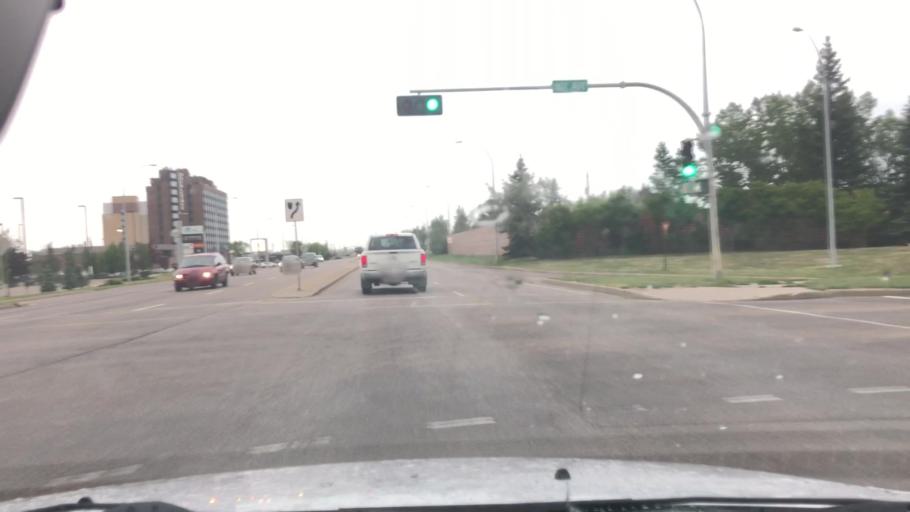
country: CA
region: Alberta
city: St. Albert
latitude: 53.5519
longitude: -113.6084
